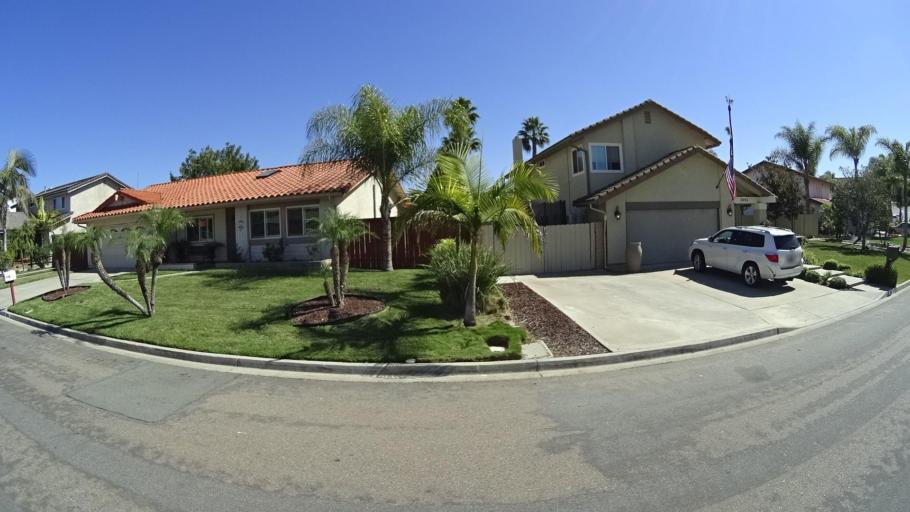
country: US
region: California
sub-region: San Diego County
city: Bonita
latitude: 32.6702
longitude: -117.0012
